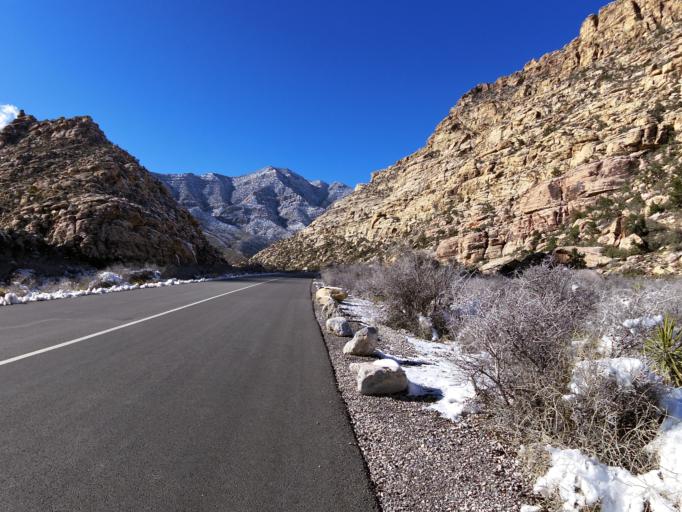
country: US
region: Nevada
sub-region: Clark County
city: Summerlin South
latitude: 36.1592
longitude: -115.4970
